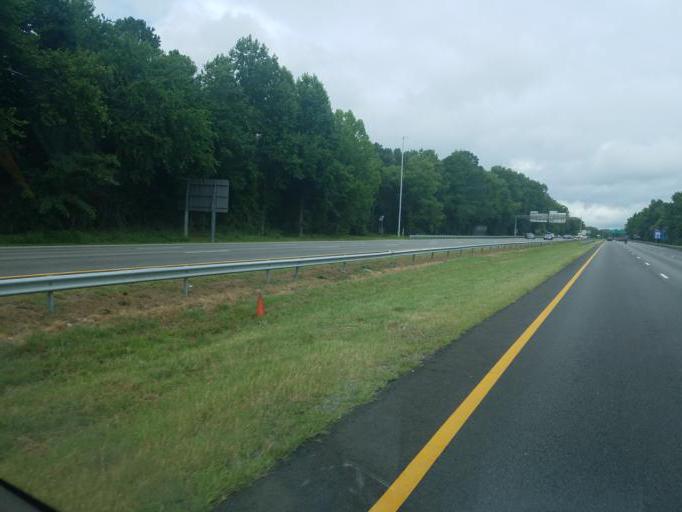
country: US
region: Virginia
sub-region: Henrico County
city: Chamberlayne
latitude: 37.6248
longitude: -77.4462
